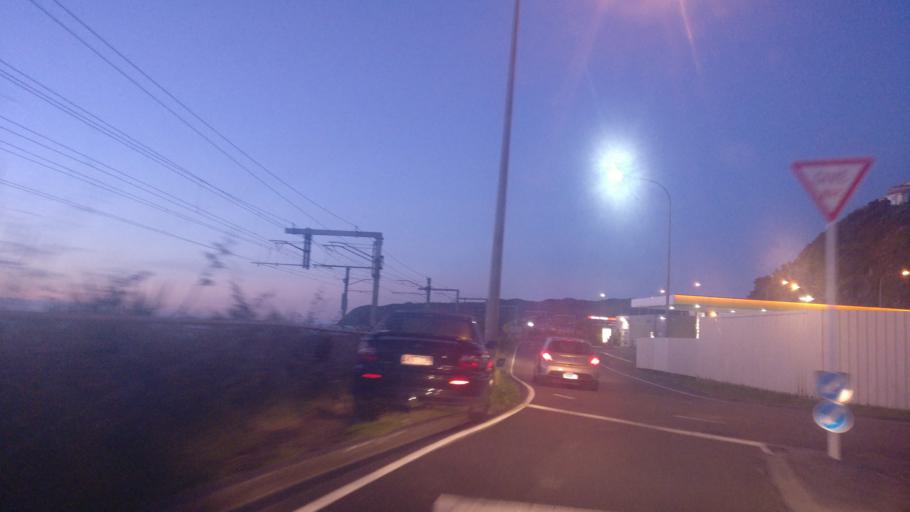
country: NZ
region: Wellington
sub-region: Porirua City
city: Porirua
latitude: -41.0922
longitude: 174.8674
